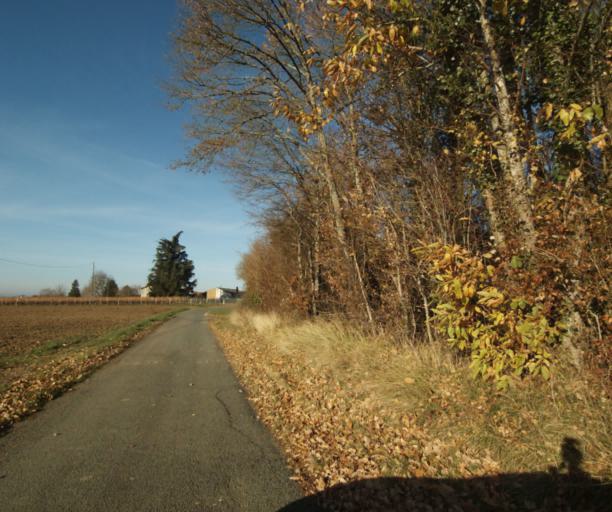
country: FR
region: Poitou-Charentes
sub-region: Departement de la Charente-Maritime
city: Cherac
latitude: 45.7126
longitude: -0.4708
